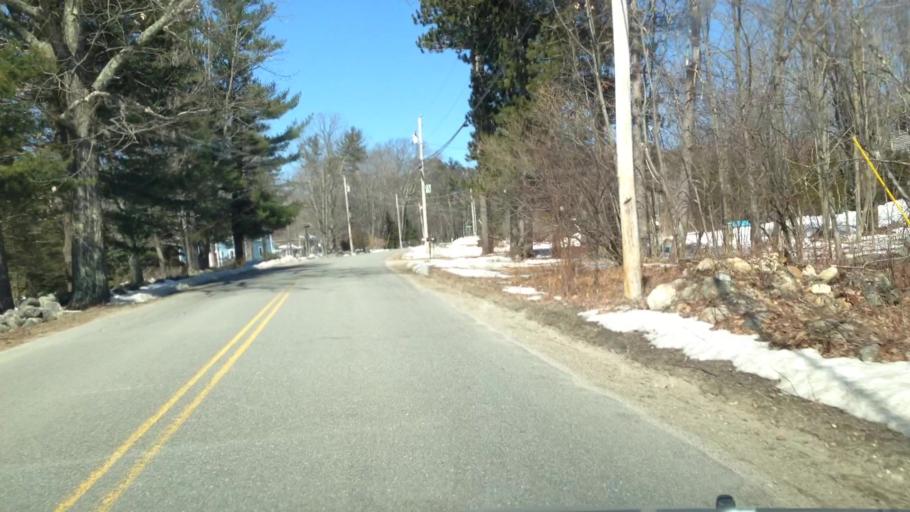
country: US
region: New Hampshire
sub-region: Hillsborough County
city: New Boston
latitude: 42.9881
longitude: -71.6489
